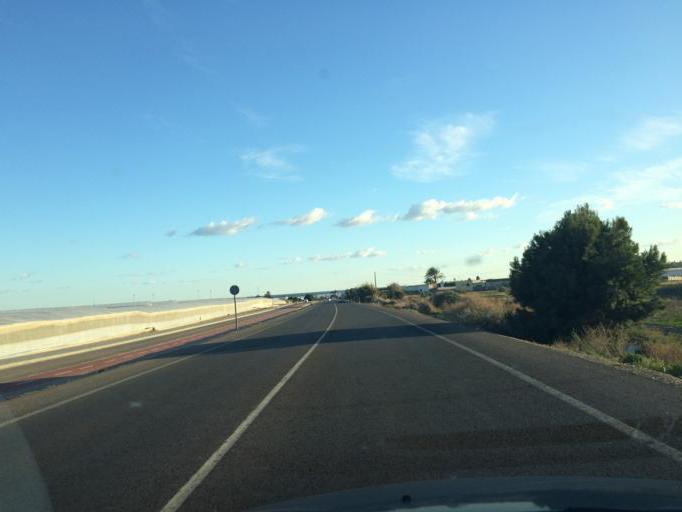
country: ES
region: Andalusia
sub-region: Provincia de Almeria
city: Almeria
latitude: 36.8377
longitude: -2.4175
